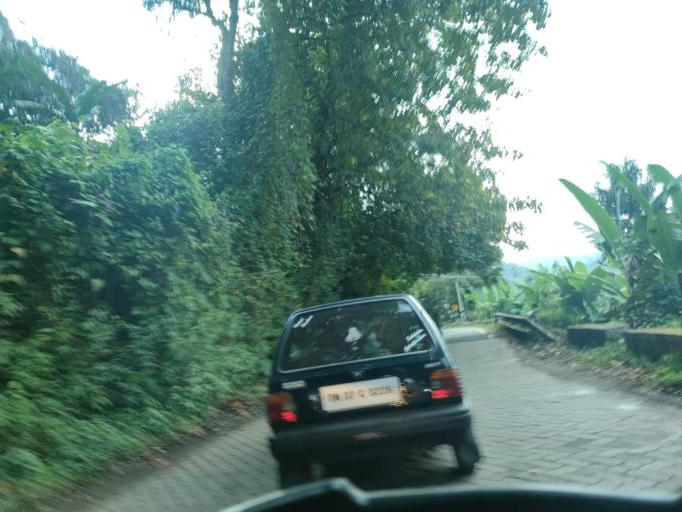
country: IN
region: Tamil Nadu
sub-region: Dindigul
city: Kodaikanal
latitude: 10.2586
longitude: 77.5335
